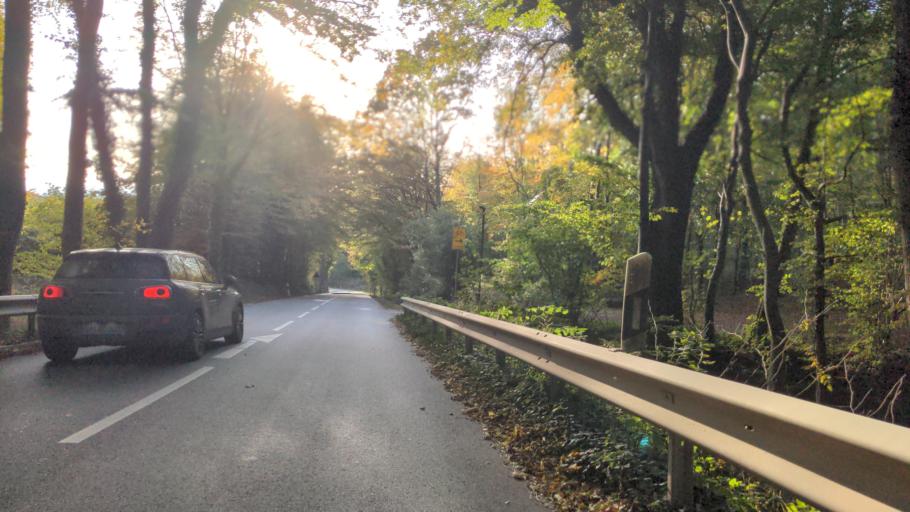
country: DE
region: Schleswig-Holstein
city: Kirchnuchel
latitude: 54.1971
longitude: 10.6478
